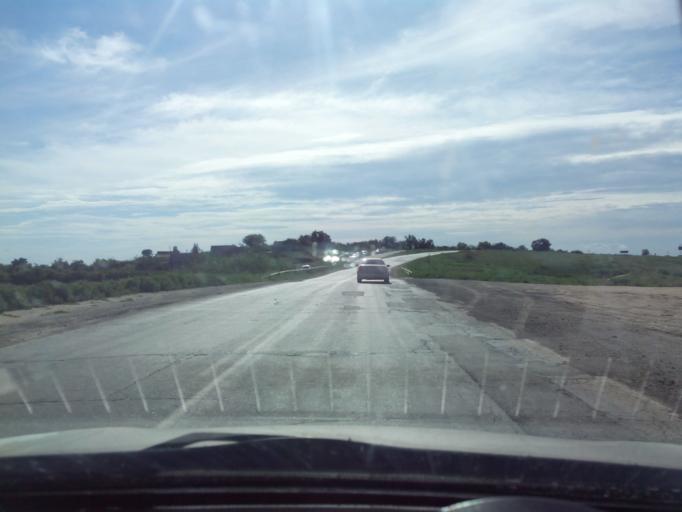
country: RU
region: Astrakhan
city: Znamensk
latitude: 48.5752
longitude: 45.7226
